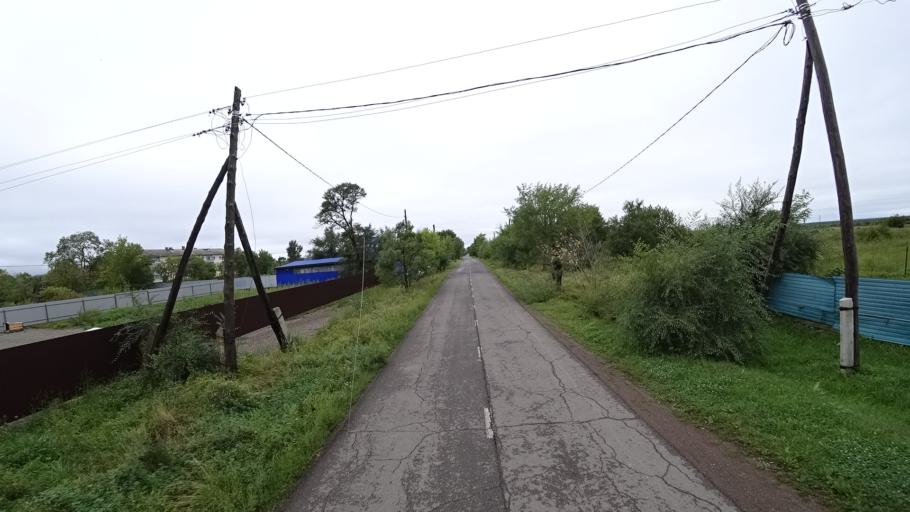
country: RU
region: Primorskiy
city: Monastyrishche
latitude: 44.2007
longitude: 132.4948
